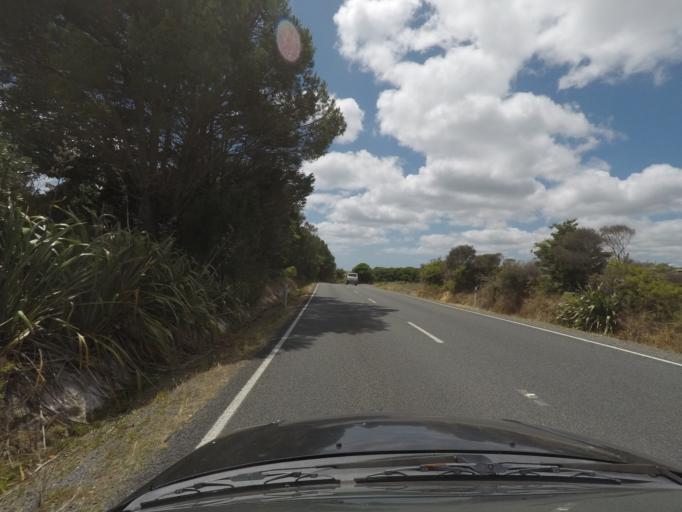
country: NZ
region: Northland
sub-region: Whangarei
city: Ruakaka
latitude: -36.0152
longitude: 174.4871
